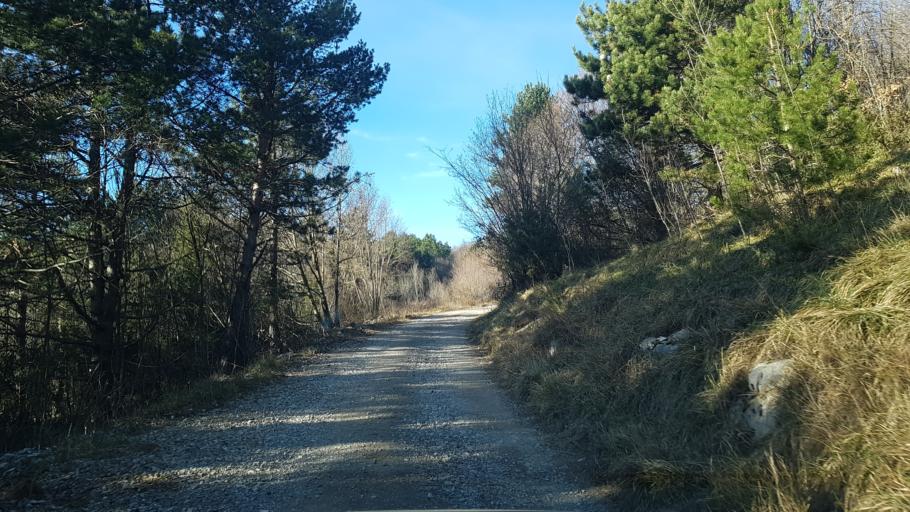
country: SI
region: Nova Gorica
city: Kromberk
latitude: 46.0147
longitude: 13.7029
